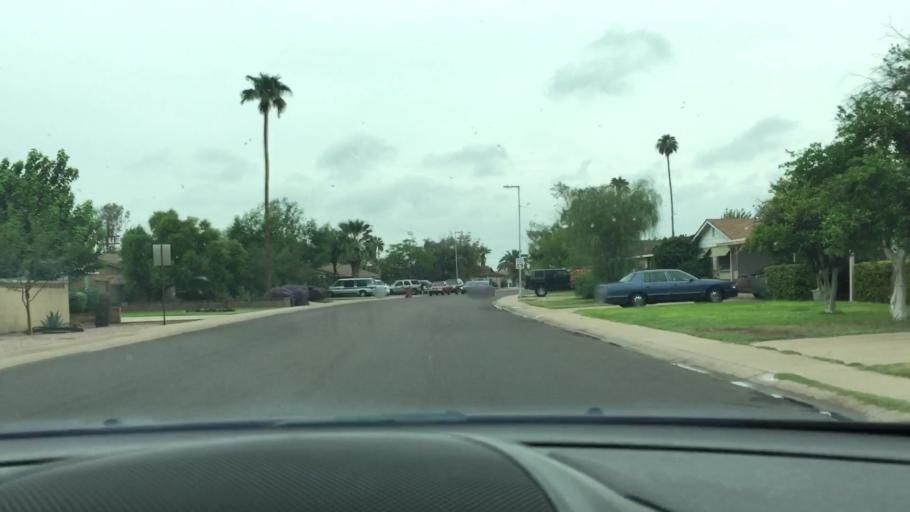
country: US
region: Arizona
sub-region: Maricopa County
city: Tempe
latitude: 33.4602
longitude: -111.9213
